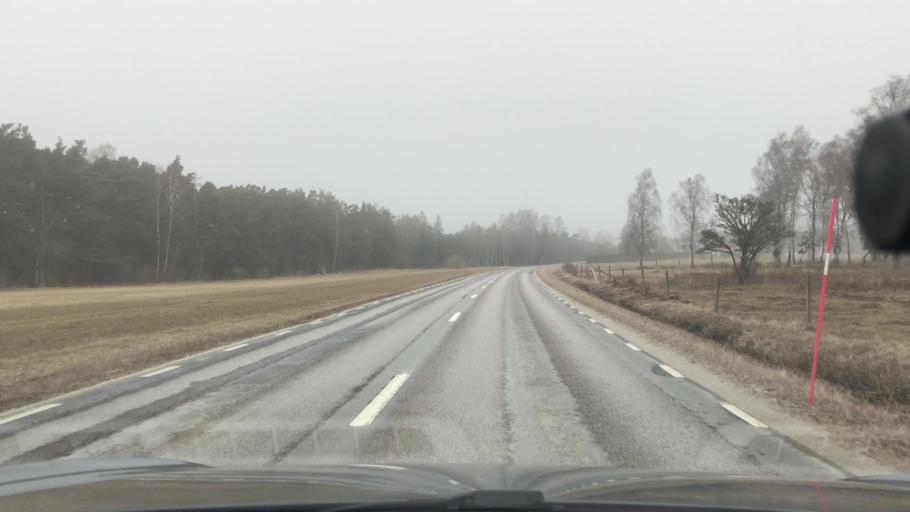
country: SE
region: Gotland
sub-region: Gotland
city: Hemse
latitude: 57.3255
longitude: 18.3823
